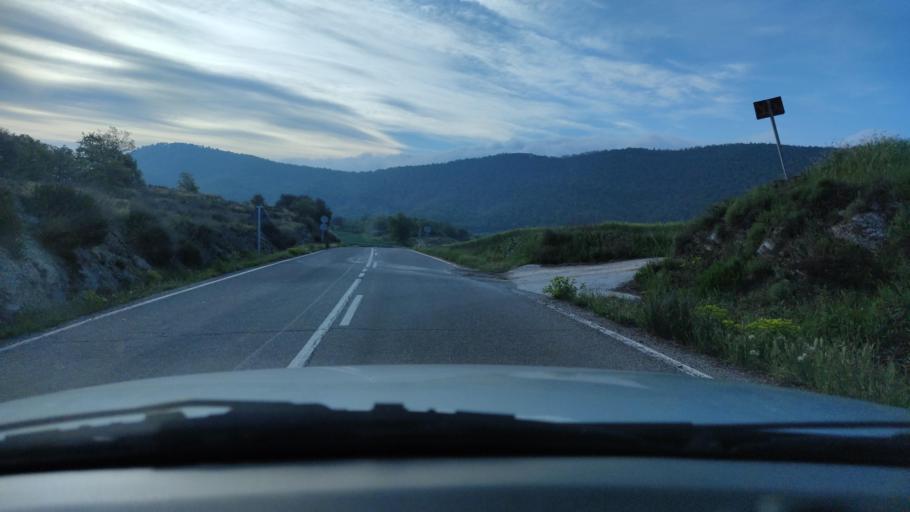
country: ES
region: Catalonia
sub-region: Provincia de Lleida
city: Ponts
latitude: 41.8910
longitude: 1.1803
